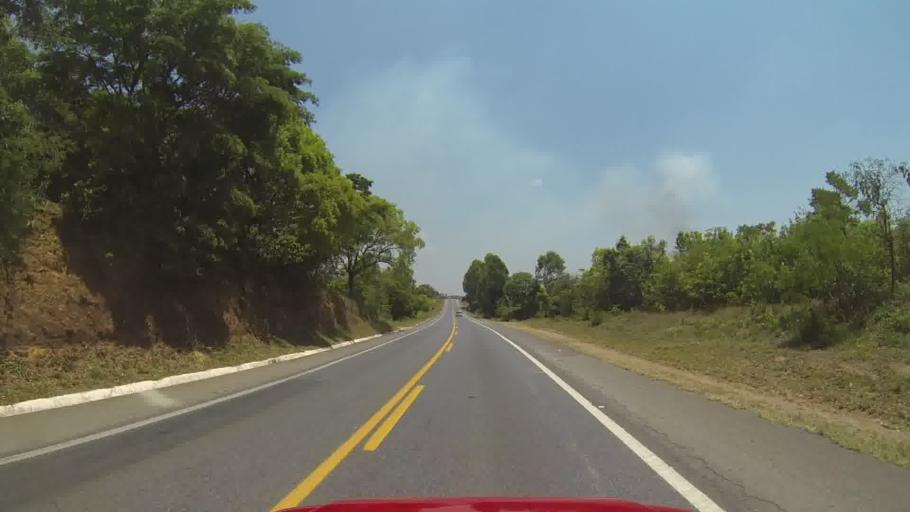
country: BR
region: Minas Gerais
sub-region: Itapecerica
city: Itapecerica
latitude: -20.3424
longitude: -45.2627
